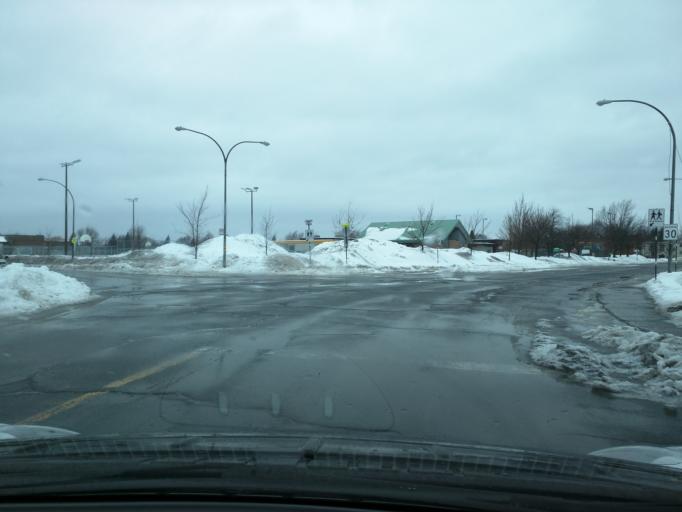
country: CA
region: Quebec
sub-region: Monteregie
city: Longueuil
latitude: 45.5246
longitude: -73.4591
